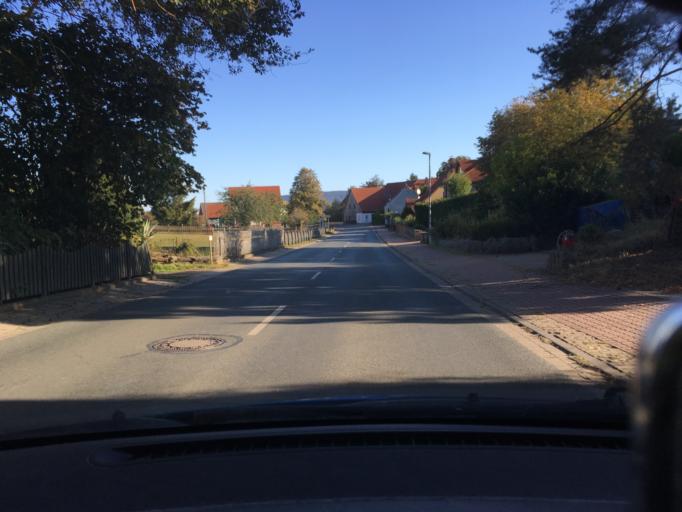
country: DE
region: Lower Saxony
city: Hulsede
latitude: 52.2410
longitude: 9.3744
